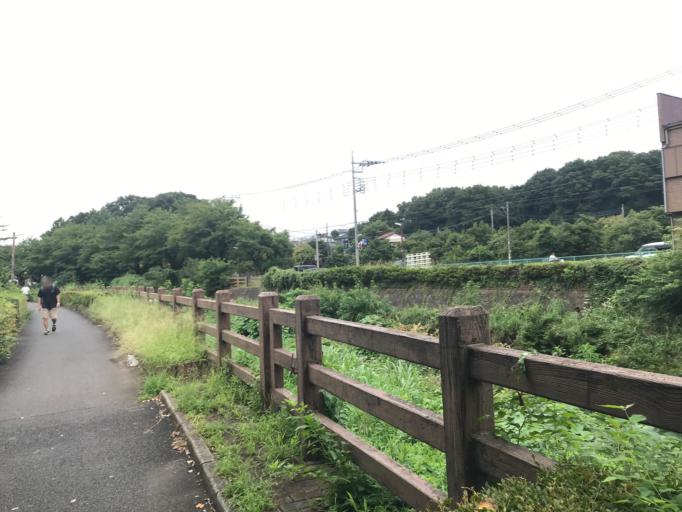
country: JP
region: Tokyo
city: Tanashicho
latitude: 35.7660
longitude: 139.5383
